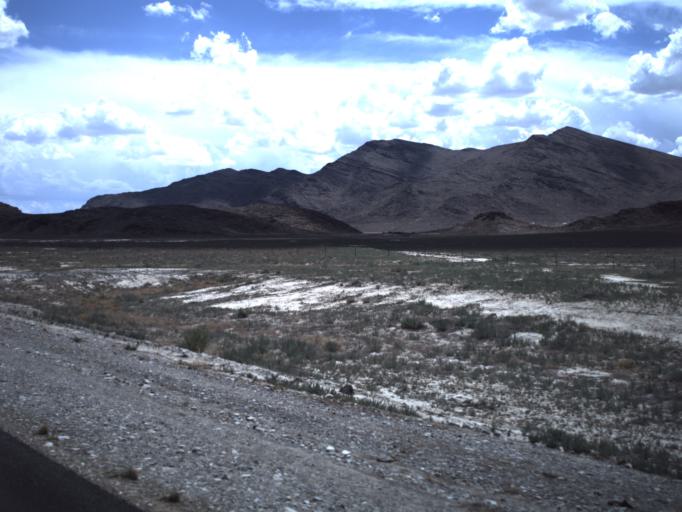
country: US
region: Utah
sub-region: Beaver County
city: Milford
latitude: 39.0617
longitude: -113.4405
